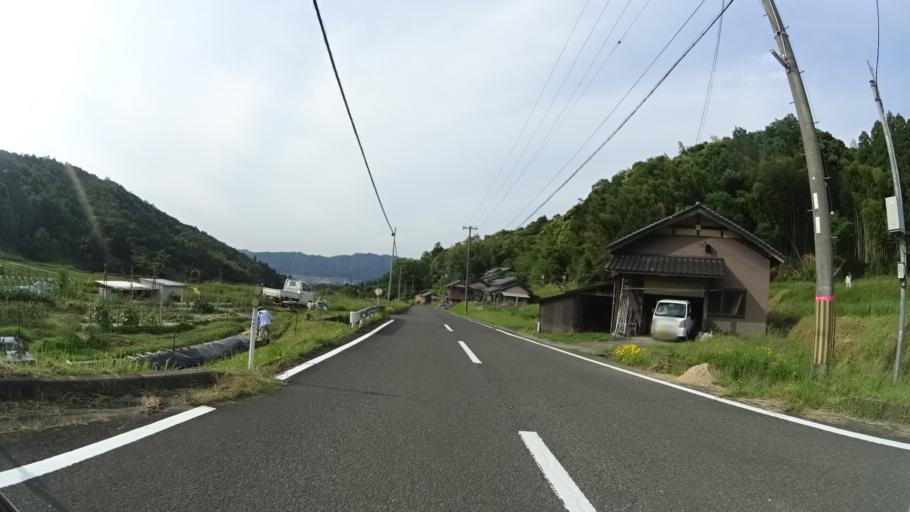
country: JP
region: Kyoto
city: Miyazu
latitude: 35.5102
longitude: 135.1275
